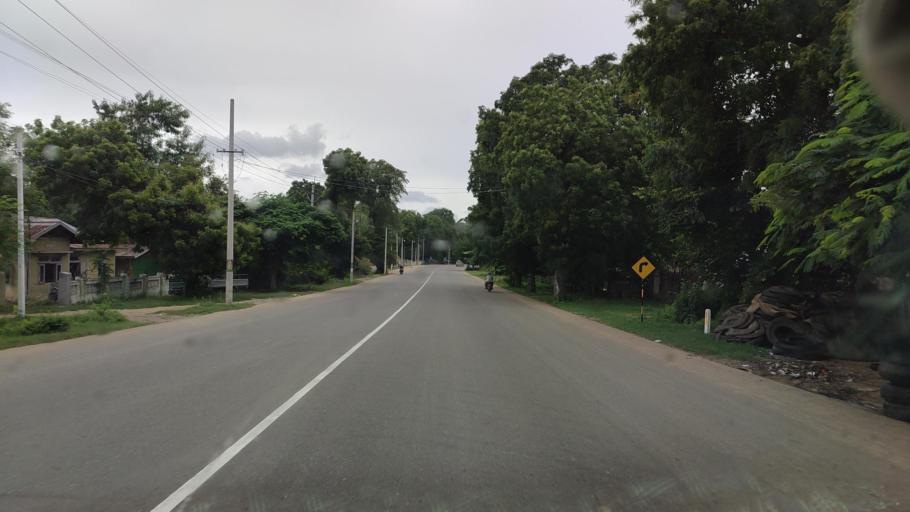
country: MM
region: Mandalay
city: Meiktila
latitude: 20.8073
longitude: 95.9072
